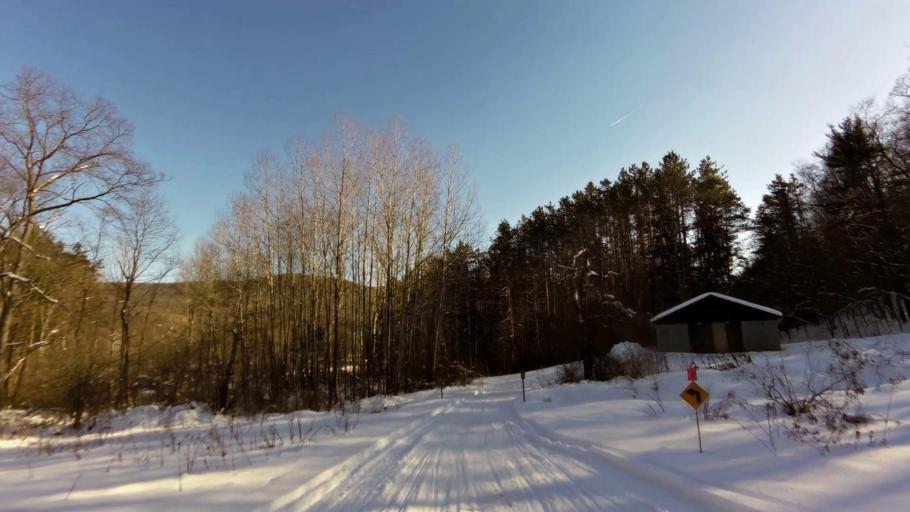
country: US
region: New York
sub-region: Cattaraugus County
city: Salamanca
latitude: 42.0750
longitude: -78.7136
